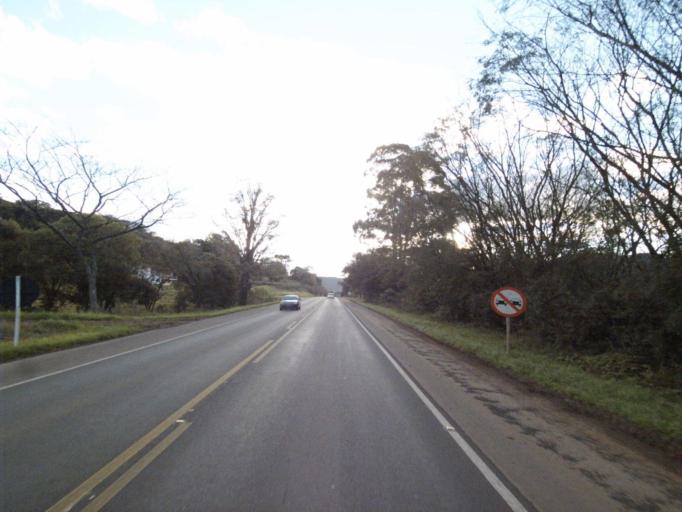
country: BR
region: Santa Catarina
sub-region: Joacaba
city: Joacaba
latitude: -27.2876
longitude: -51.4253
